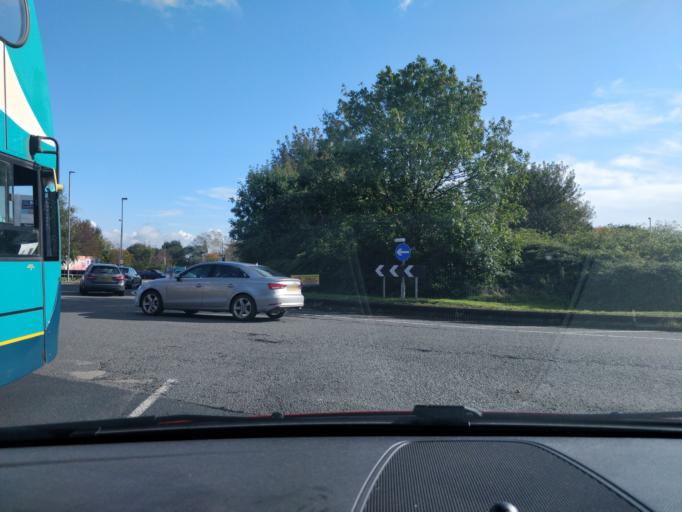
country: GB
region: England
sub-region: Sefton
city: Southport
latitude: 53.6335
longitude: -2.9707
